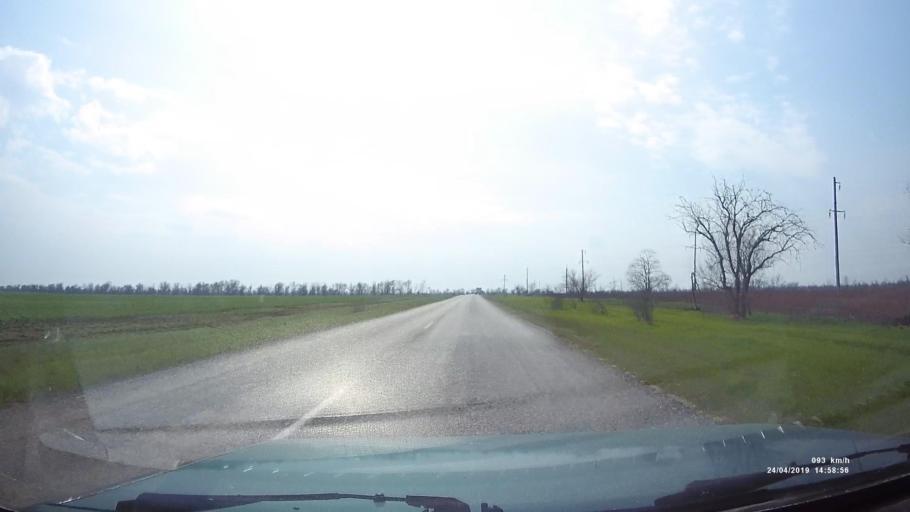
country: RU
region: Rostov
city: Remontnoye
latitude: 46.5683
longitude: 43.5860
